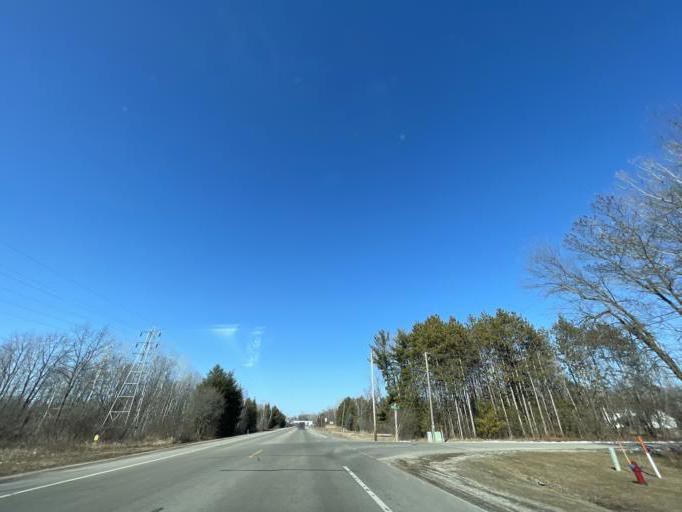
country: US
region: Wisconsin
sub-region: Brown County
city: Suamico
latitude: 44.5980
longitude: -88.0779
